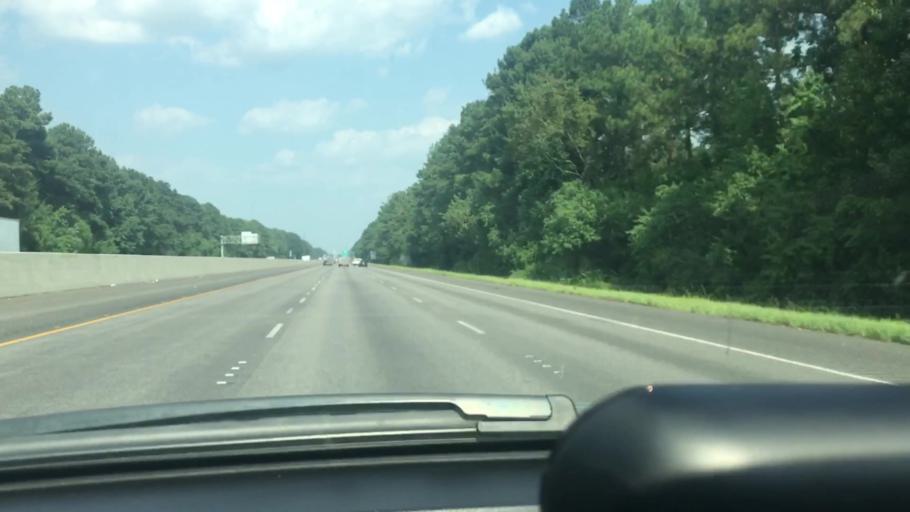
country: US
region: Louisiana
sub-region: Livingston Parish
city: Walker
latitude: 30.4696
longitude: -90.8839
